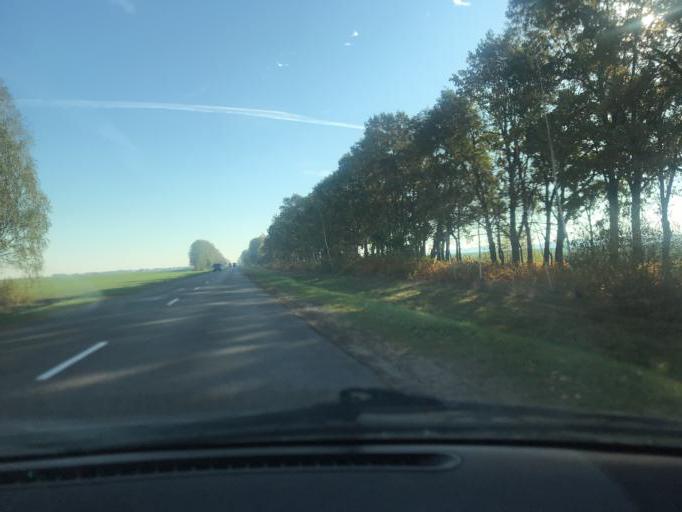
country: BY
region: Brest
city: Ivanava
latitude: 52.1456
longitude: 25.4734
